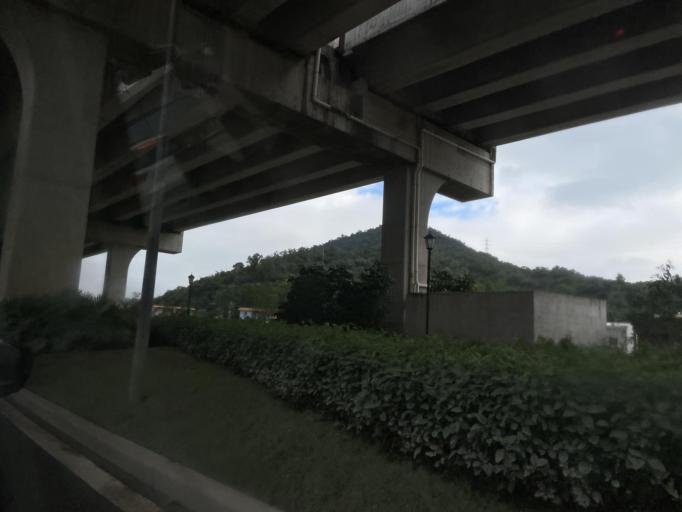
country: CN
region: Guangdong
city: Nanping
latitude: 22.1791
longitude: 113.4630
